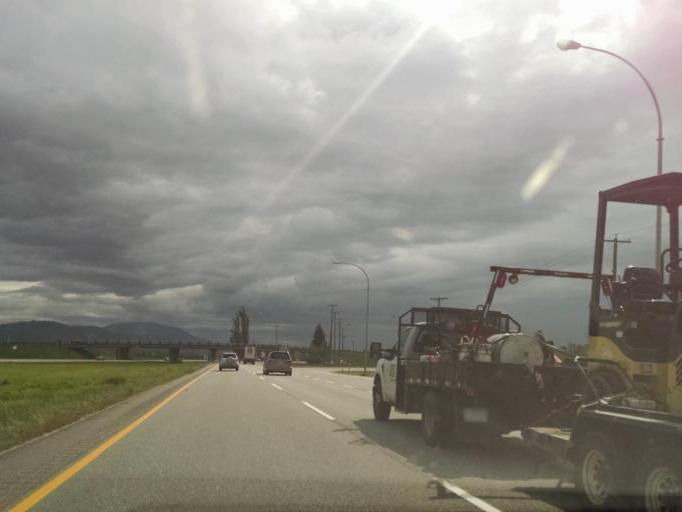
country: CA
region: British Columbia
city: Abbotsford
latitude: 49.0919
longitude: -122.1233
